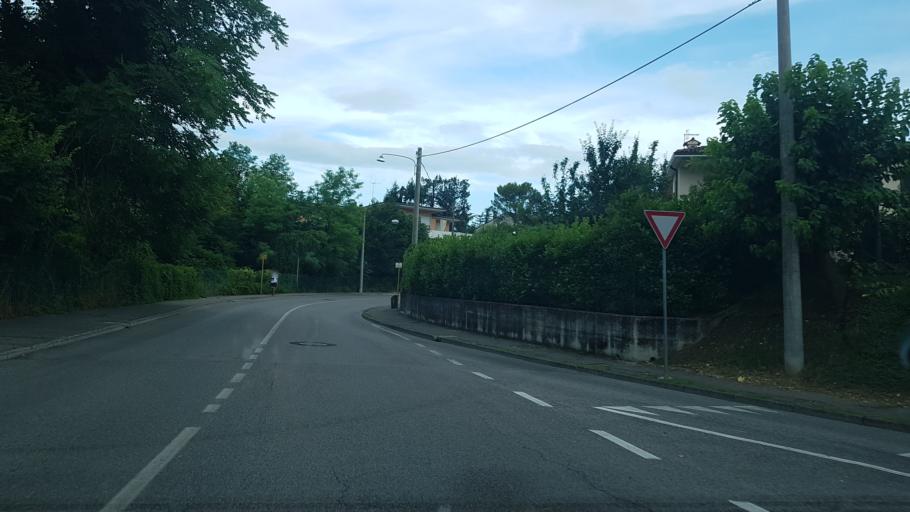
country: IT
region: Friuli Venezia Giulia
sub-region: Provincia di Gorizia
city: Gorizia
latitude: 45.9450
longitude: 13.6087
